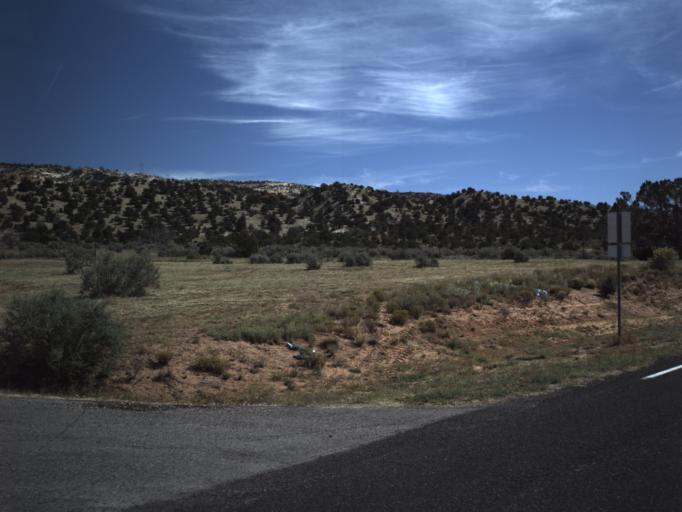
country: US
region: Utah
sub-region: Wayne County
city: Loa
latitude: 37.7614
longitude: -111.5789
